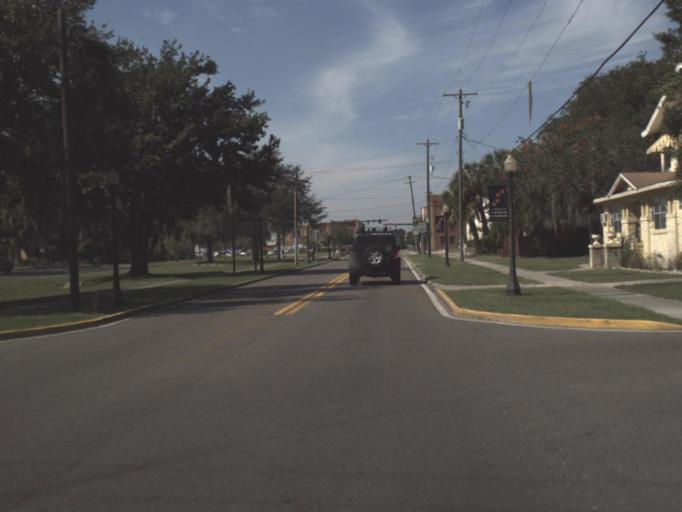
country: US
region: Florida
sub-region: Hardee County
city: Wauchula
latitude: 27.5483
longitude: -81.8082
